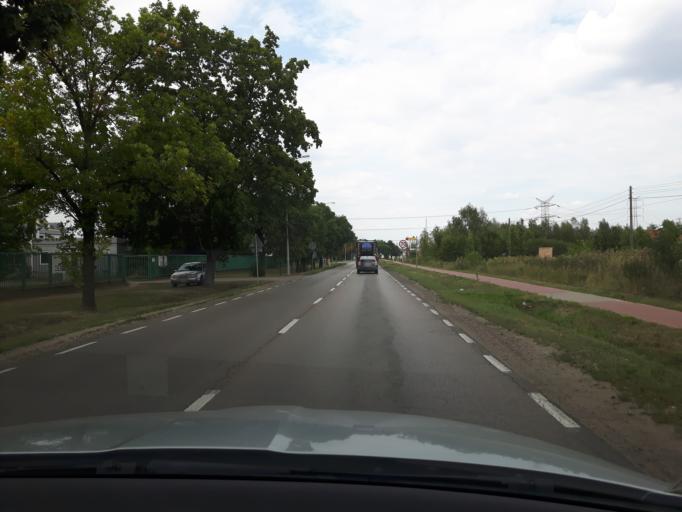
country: PL
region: Masovian Voivodeship
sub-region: Powiat legionowski
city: Stanislawow Pierwszy
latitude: 52.3679
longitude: 21.0288
